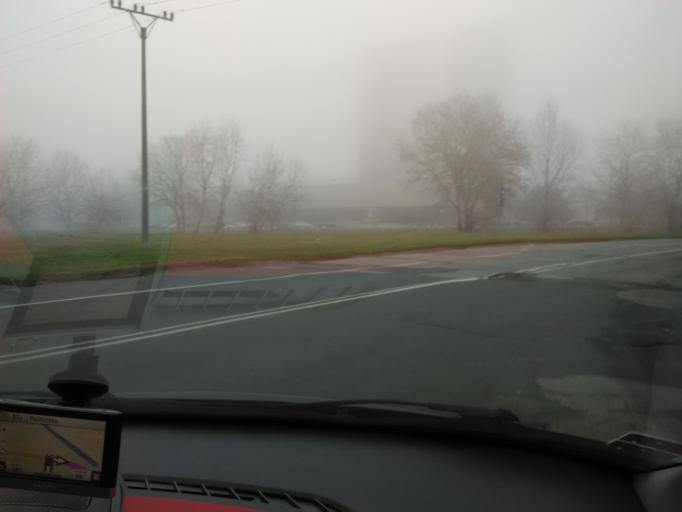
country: SK
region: Bratislavsky
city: Bratislava
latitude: 48.1108
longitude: 17.1084
